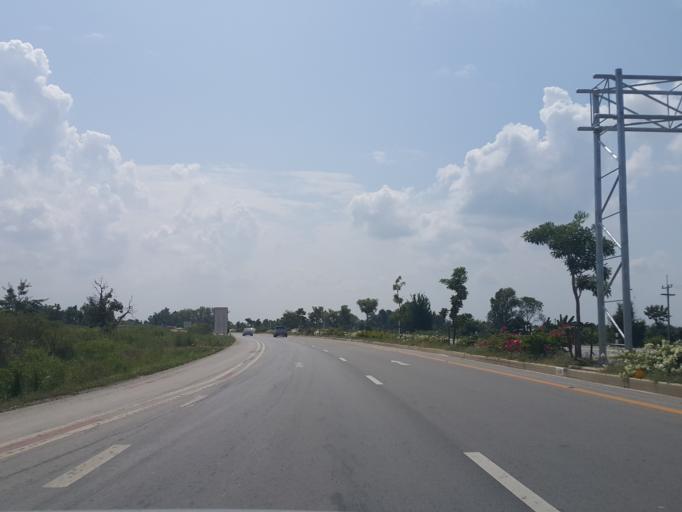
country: TH
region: Chiang Mai
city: Mae Wang
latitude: 18.5992
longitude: 98.8340
